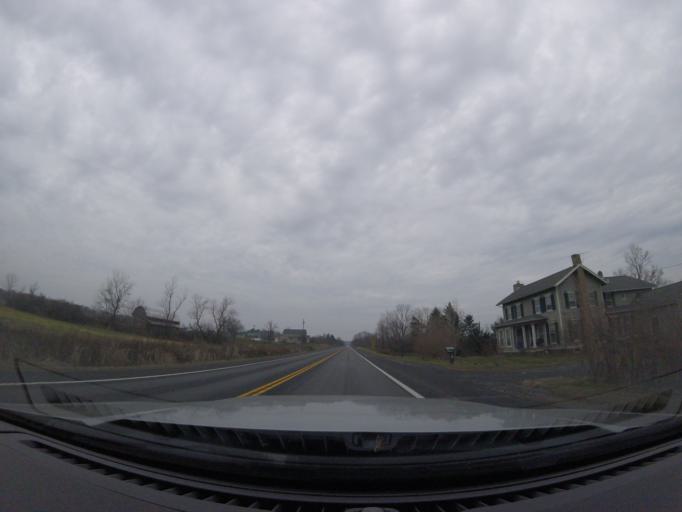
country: US
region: New York
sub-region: Schuyler County
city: Watkins Glen
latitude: 42.4561
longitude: -76.9112
